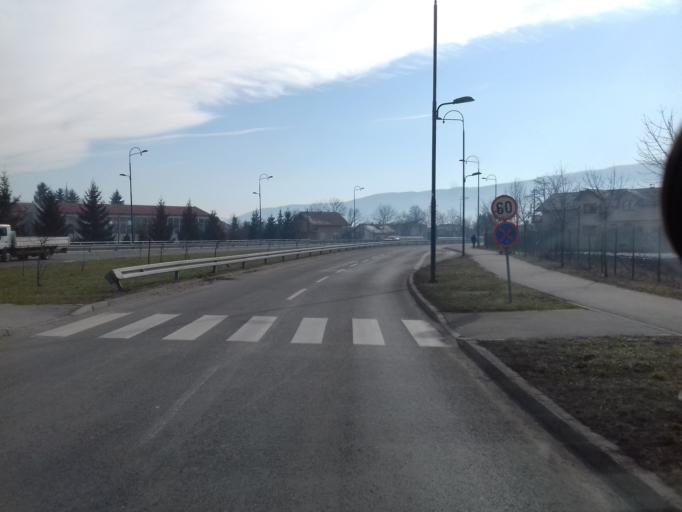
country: BA
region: Federation of Bosnia and Herzegovina
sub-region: Kanton Sarajevo
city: Sarajevo
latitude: 43.8239
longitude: 18.3192
